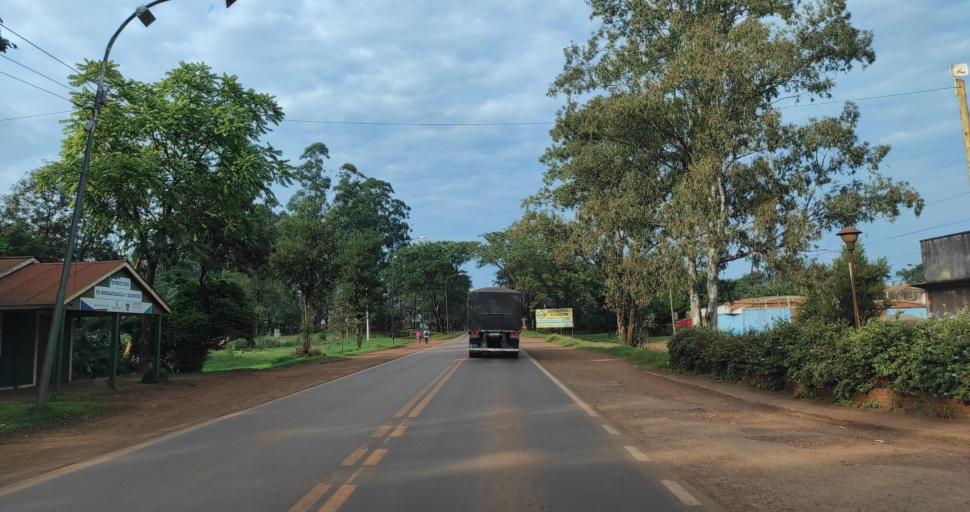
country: AR
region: Corrientes
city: Gobernador Ingeniero Valentin Virasoro
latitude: -28.0380
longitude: -56.0132
